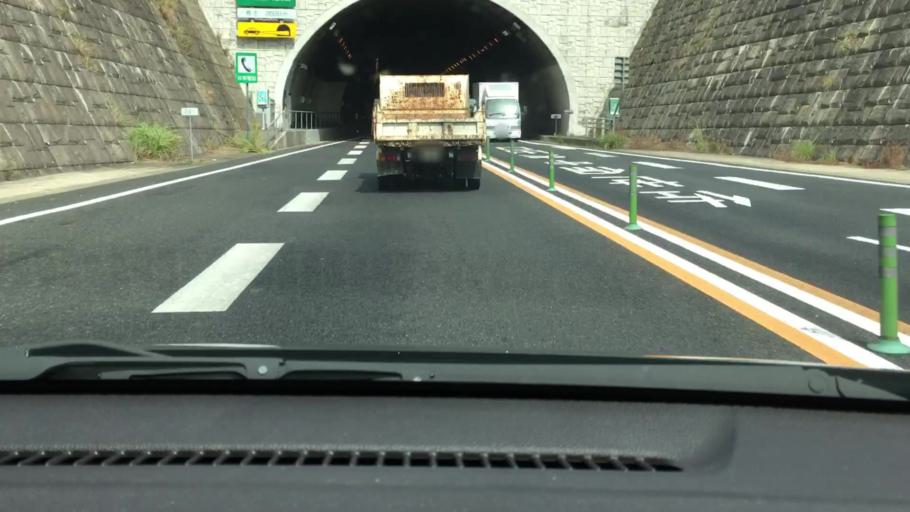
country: JP
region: Nagasaki
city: Sasebo
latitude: 33.1746
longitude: 129.7103
